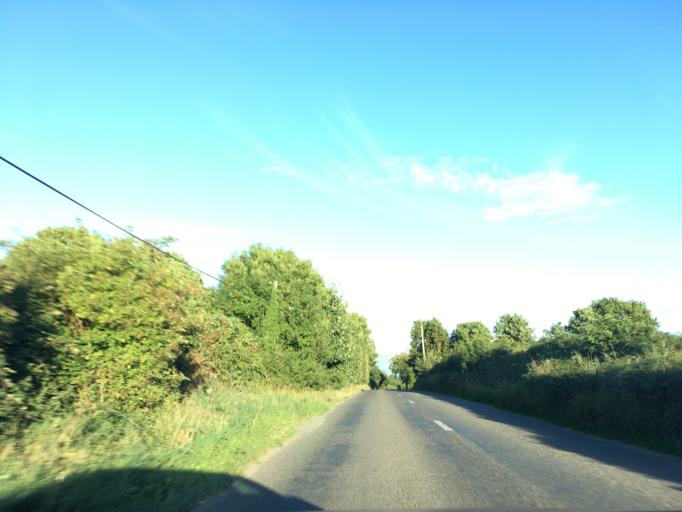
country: IE
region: Munster
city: Cashel
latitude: 52.4836
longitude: -7.9397
